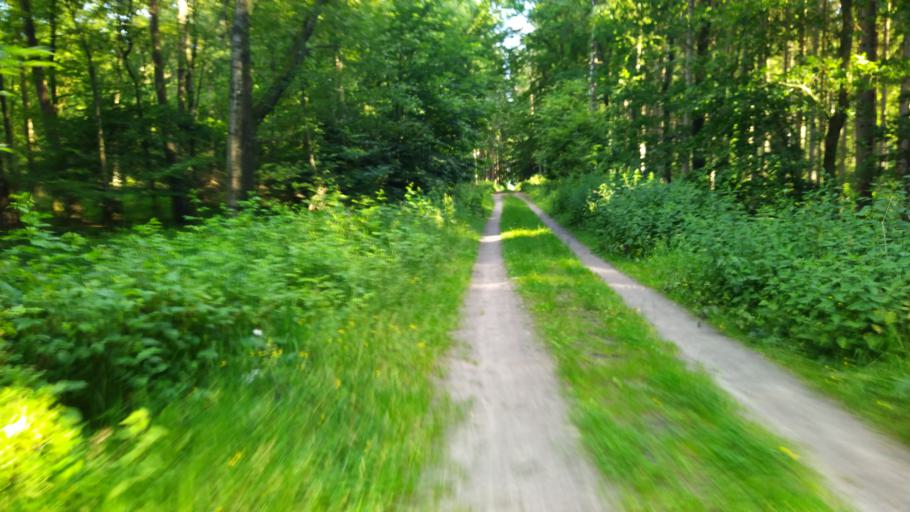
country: DE
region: Lower Saxony
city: Lintig
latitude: 53.5965
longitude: 8.8944
